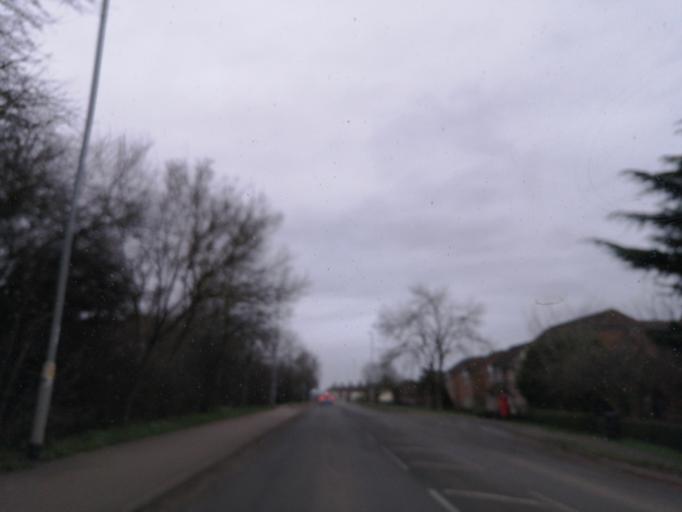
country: GB
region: England
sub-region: Cambridgeshire
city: Yaxley
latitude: 52.5208
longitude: -0.2476
